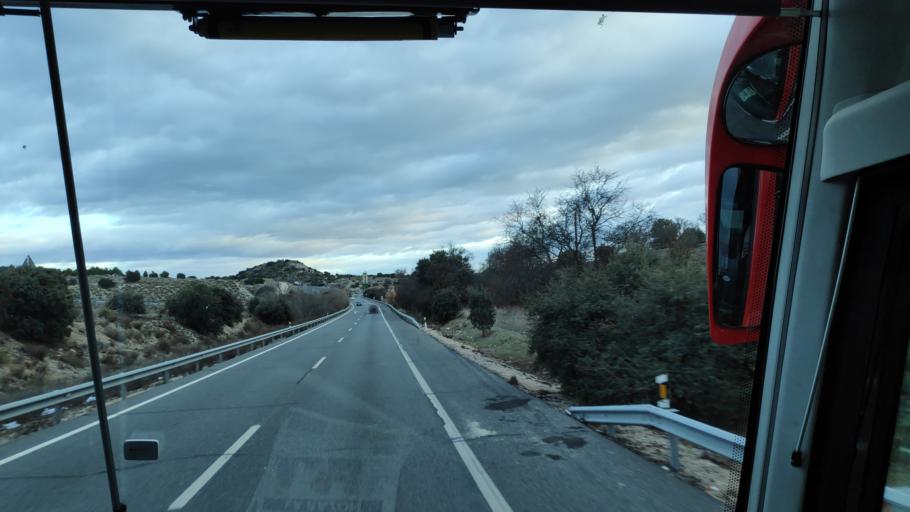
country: ES
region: Madrid
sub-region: Provincia de Madrid
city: Villarejo de Salvanes
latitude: 40.1466
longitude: -3.2175
